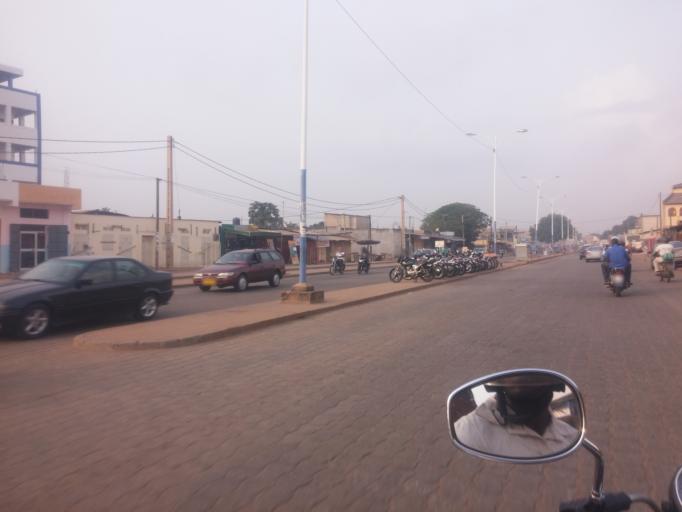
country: TG
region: Maritime
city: Lome
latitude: 6.1585
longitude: 1.2571
